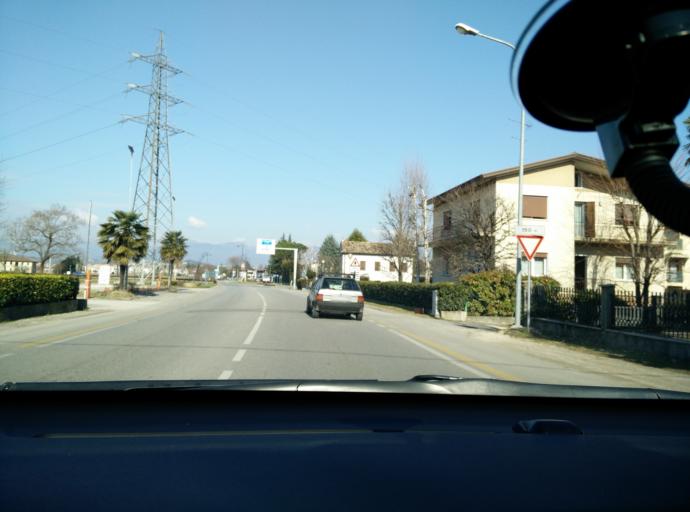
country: IT
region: Veneto
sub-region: Provincia di Treviso
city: Santa Lucia di Piave
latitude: 45.8546
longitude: 12.3072
